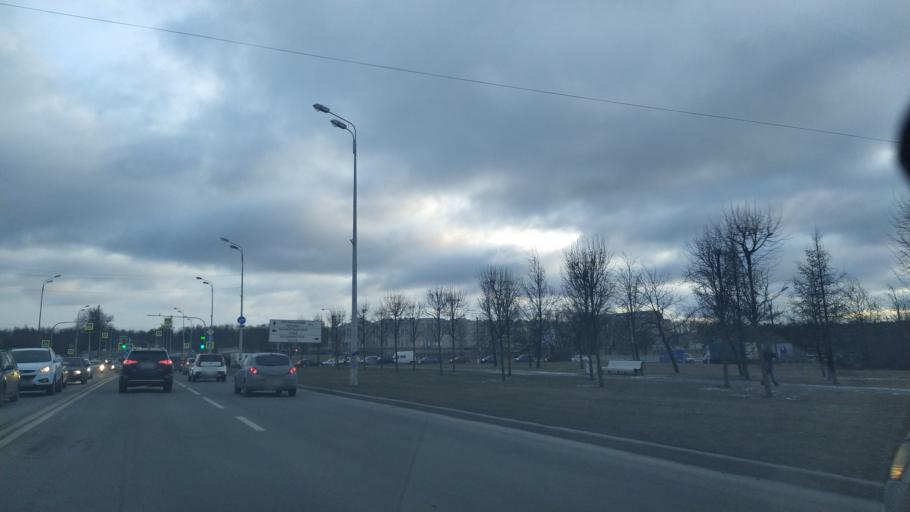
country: RU
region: St.-Petersburg
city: Pushkin
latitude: 59.7349
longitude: 30.3940
